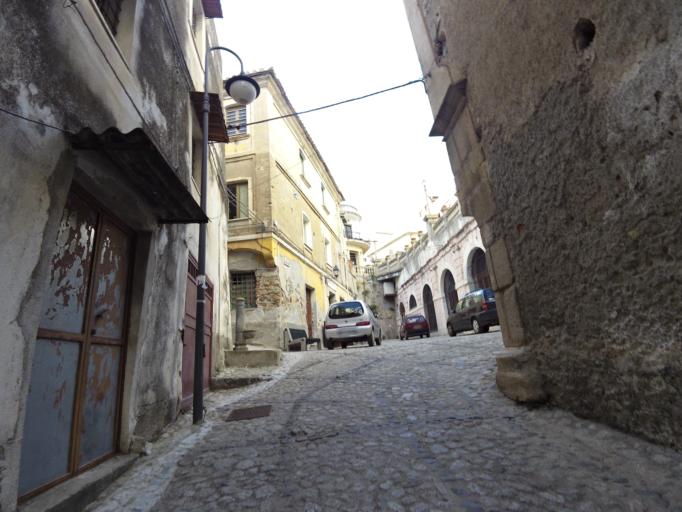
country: IT
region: Calabria
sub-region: Provincia di Reggio Calabria
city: Caulonia
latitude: 38.3813
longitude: 16.4072
